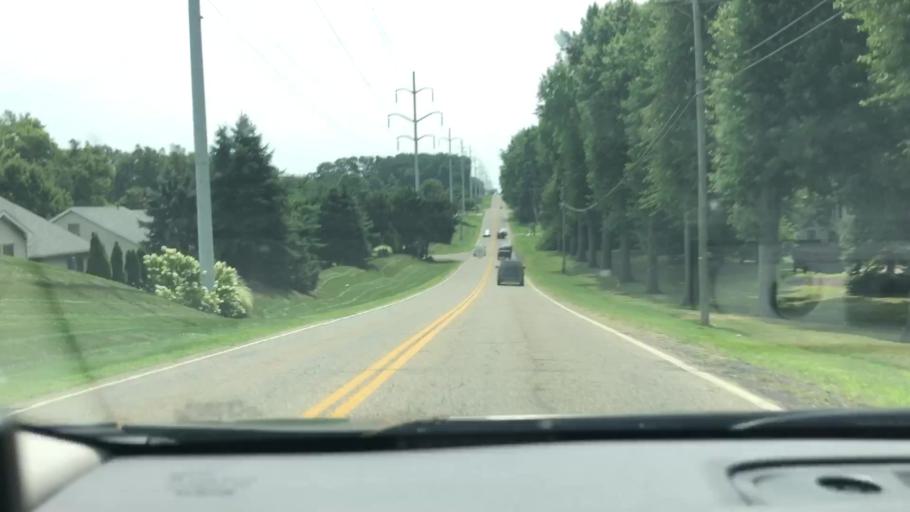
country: US
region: Ohio
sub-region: Stark County
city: Perry Heights
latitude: 40.8276
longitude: -81.4342
